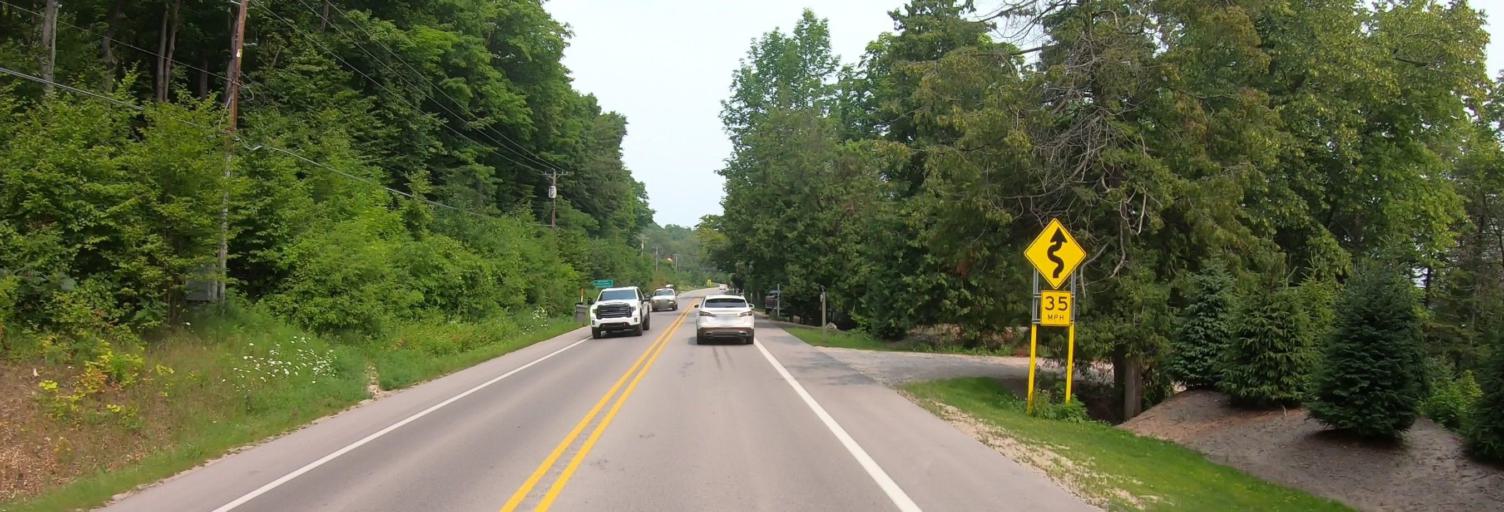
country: US
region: Michigan
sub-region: Leelanau County
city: Leland
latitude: 44.9991
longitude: -85.7718
